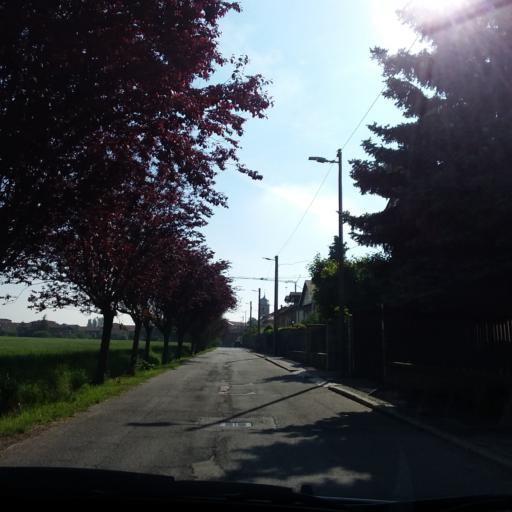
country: IT
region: Piedmont
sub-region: Provincia di Torino
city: Tetti Neirotti
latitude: 45.0505
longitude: 7.5393
